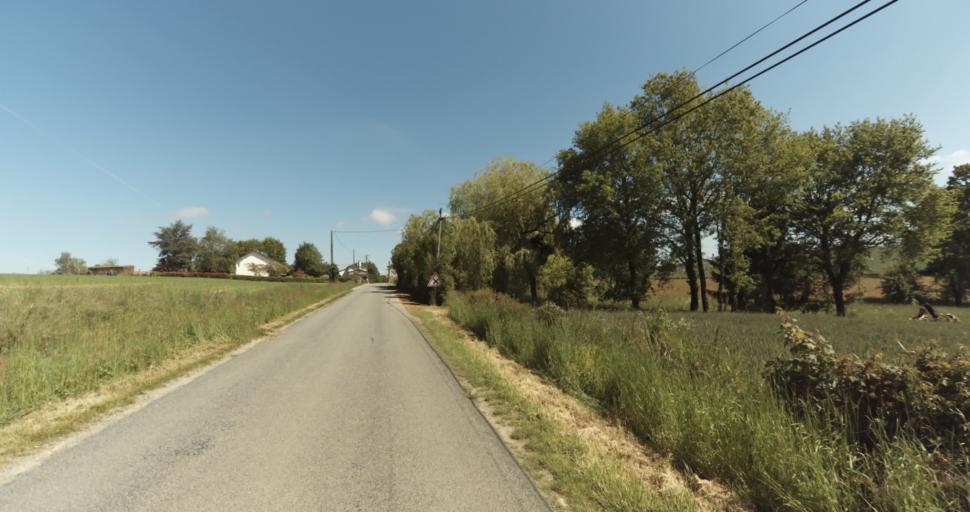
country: FR
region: Limousin
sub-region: Departement de la Haute-Vienne
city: Le Vigen
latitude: 45.7338
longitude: 1.2886
